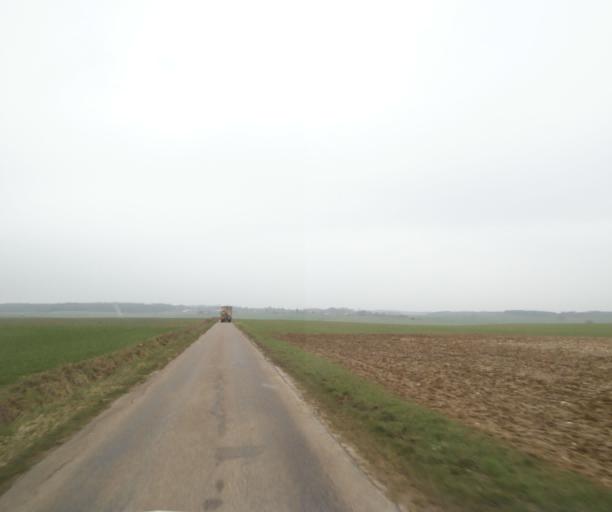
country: FR
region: Champagne-Ardenne
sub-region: Departement de la Haute-Marne
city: Chevillon
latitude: 48.5027
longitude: 5.0813
